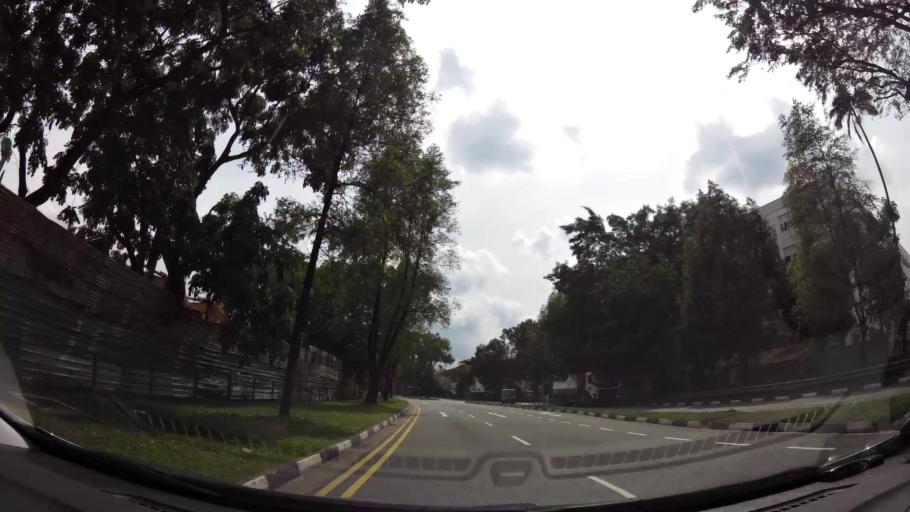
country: MY
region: Johor
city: Johor Bahru
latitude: 1.4209
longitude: 103.7430
